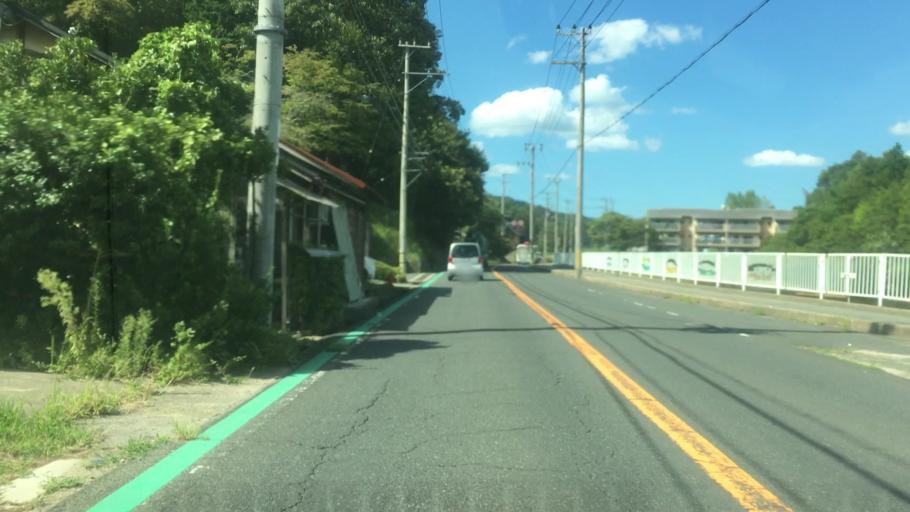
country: JP
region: Kyoto
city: Miyazu
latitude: 35.6138
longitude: 135.0541
